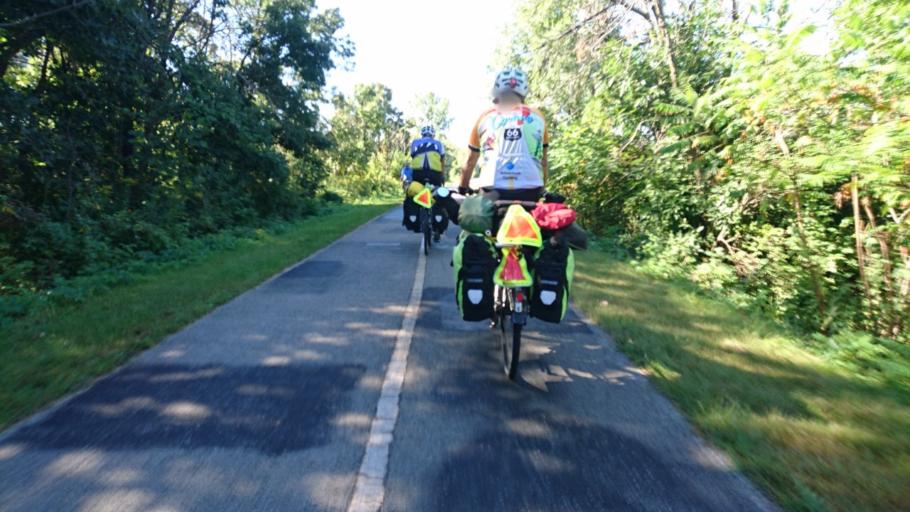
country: US
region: Indiana
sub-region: Lake County
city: Whiting
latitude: 41.6819
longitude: -87.5313
